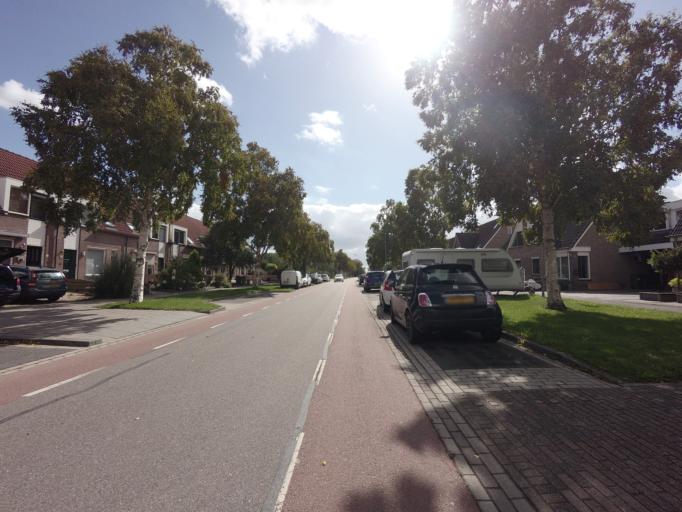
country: NL
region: North Holland
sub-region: Gemeente Purmerend
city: Purmerend
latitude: 52.5682
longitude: 4.9948
